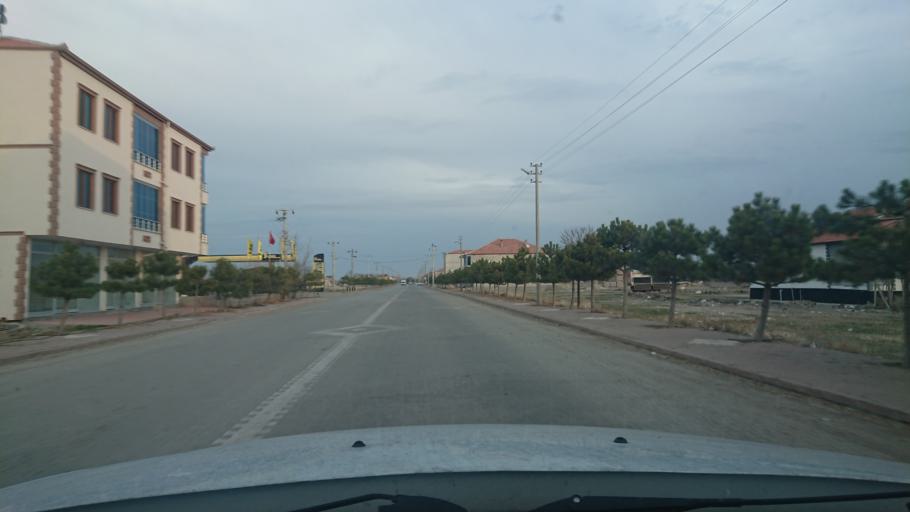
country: TR
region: Aksaray
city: Yesilova
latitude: 38.3348
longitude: 33.7515
